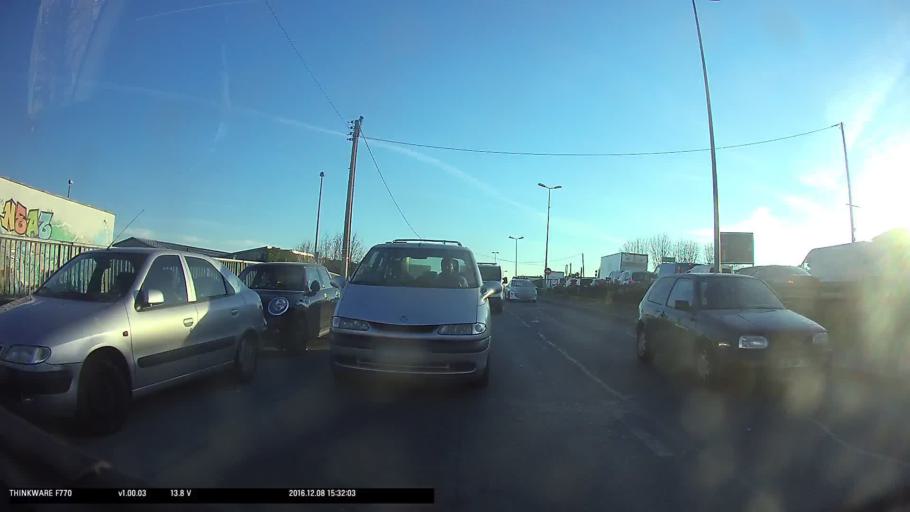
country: FR
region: Ile-de-France
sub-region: Departement de Seine-Saint-Denis
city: Bobigny
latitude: 48.9000
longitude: 2.4416
